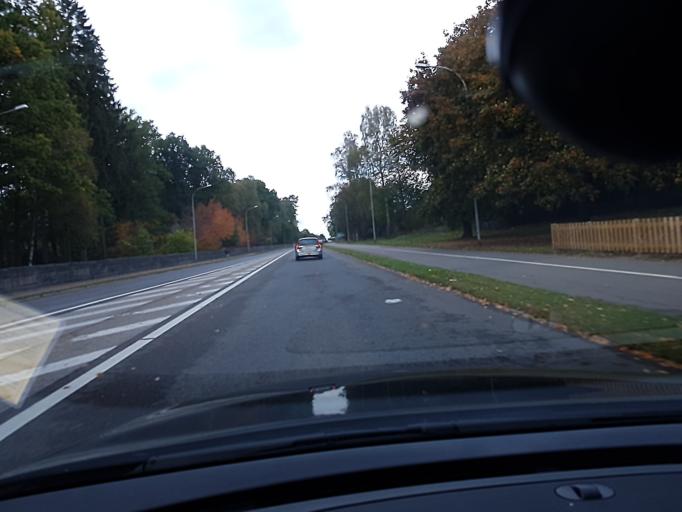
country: SE
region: Kronoberg
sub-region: Vaxjo Kommun
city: Vaexjoe
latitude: 56.8874
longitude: 14.8142
